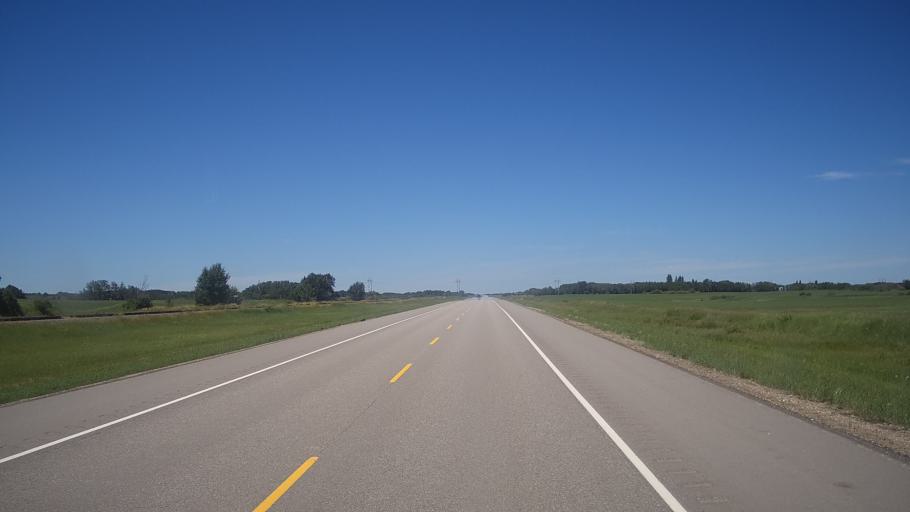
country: CA
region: Manitoba
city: Minnedosa
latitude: 50.2754
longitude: -99.9459
